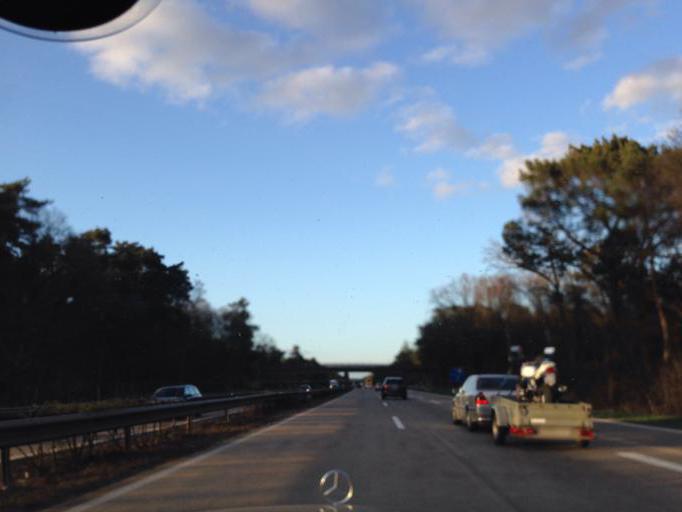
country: DE
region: Lower Saxony
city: Bad Fallingbostel
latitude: 52.9019
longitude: 9.7858
